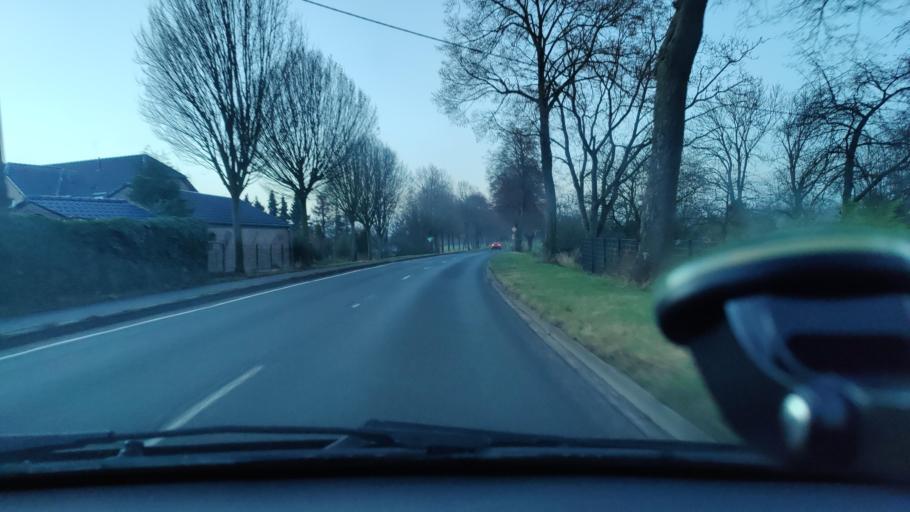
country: DE
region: North Rhine-Westphalia
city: Rheinberg
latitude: 51.5774
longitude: 6.6218
